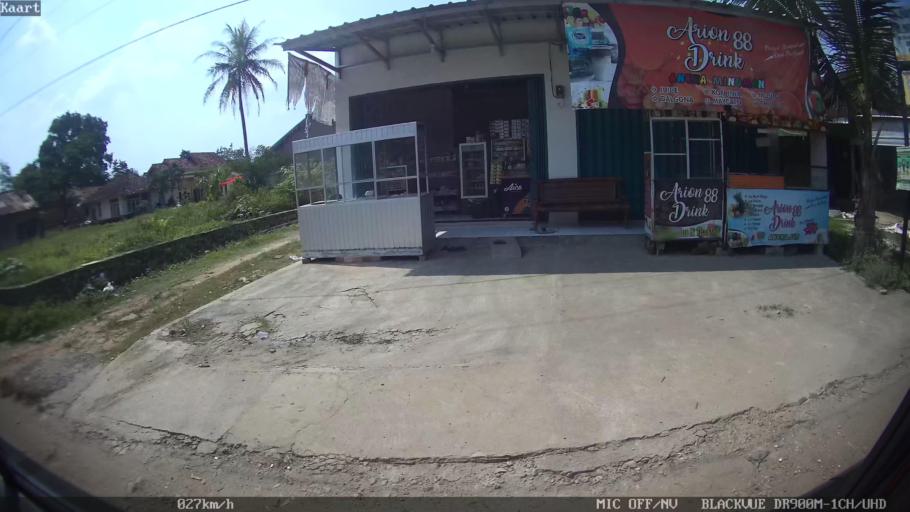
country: ID
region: Lampung
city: Natar
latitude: -5.3089
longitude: 105.2121
